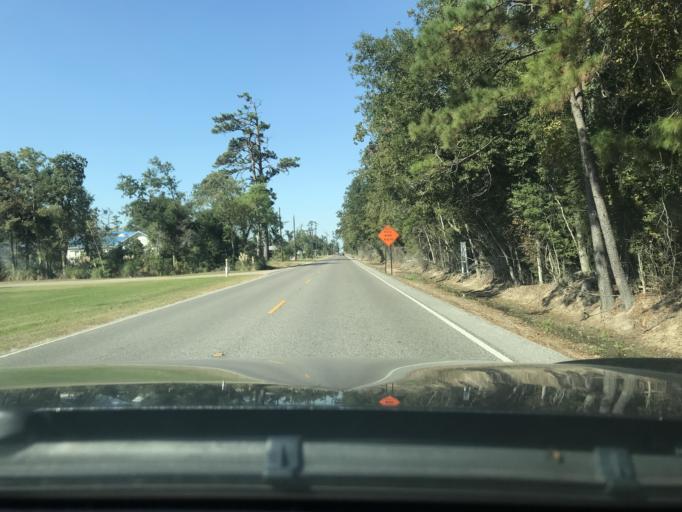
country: US
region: Louisiana
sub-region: Calcasieu Parish
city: Moss Bluff
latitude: 30.3046
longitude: -93.2001
